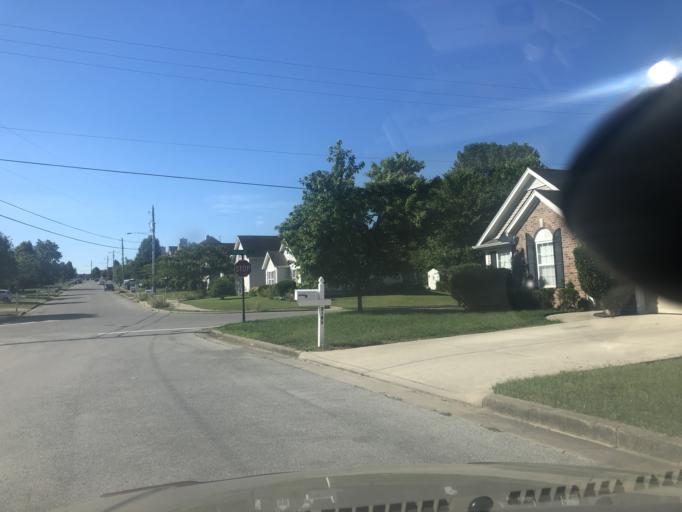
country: US
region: Tennessee
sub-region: Davidson County
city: Lakewood
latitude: 36.2473
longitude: -86.6673
